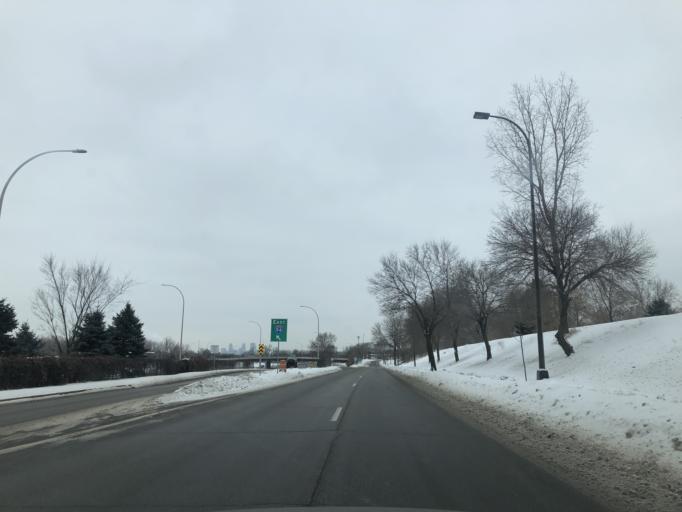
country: US
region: Minnesota
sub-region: Anoka County
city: Columbia Heights
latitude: 45.0473
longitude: -93.2851
